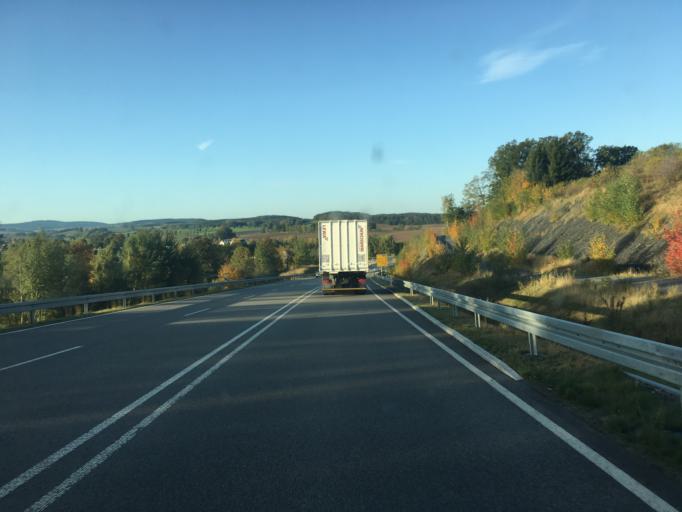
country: DE
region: Saxony
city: Kirchberg
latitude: 50.6070
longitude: 12.5523
